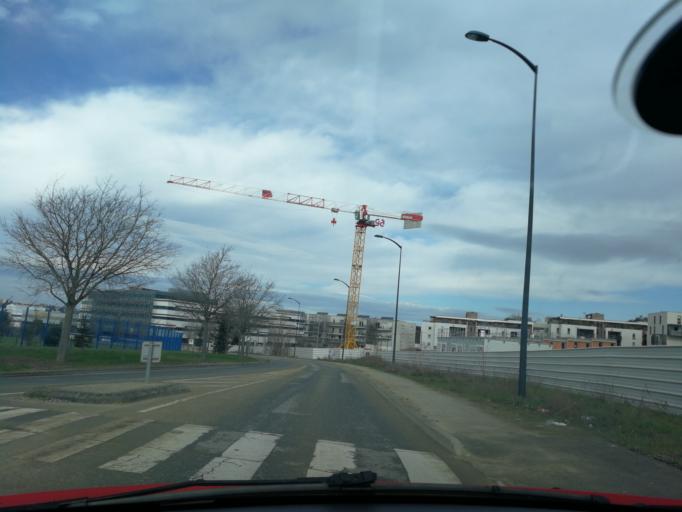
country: FR
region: Midi-Pyrenees
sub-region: Departement de la Haute-Garonne
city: Balma
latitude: 43.6228
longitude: 1.4929
